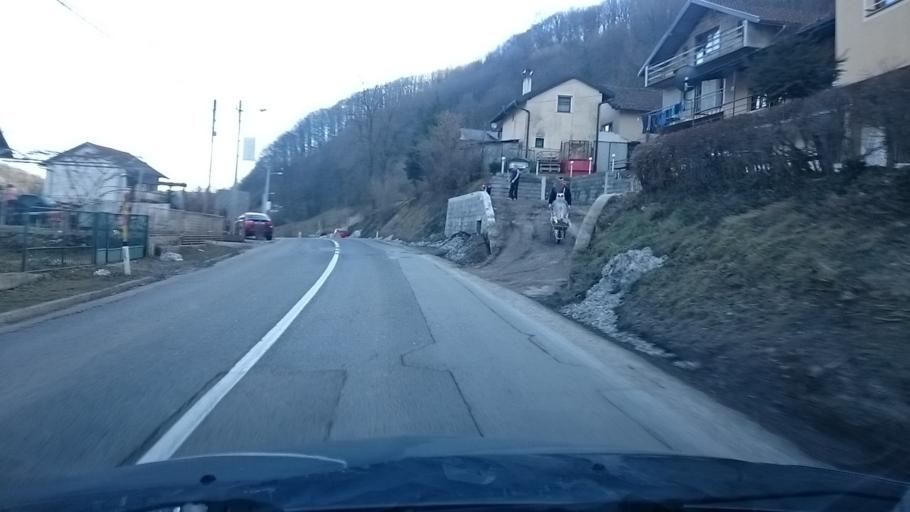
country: BA
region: Republika Srpska
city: Hiseti
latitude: 44.7227
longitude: 17.1570
